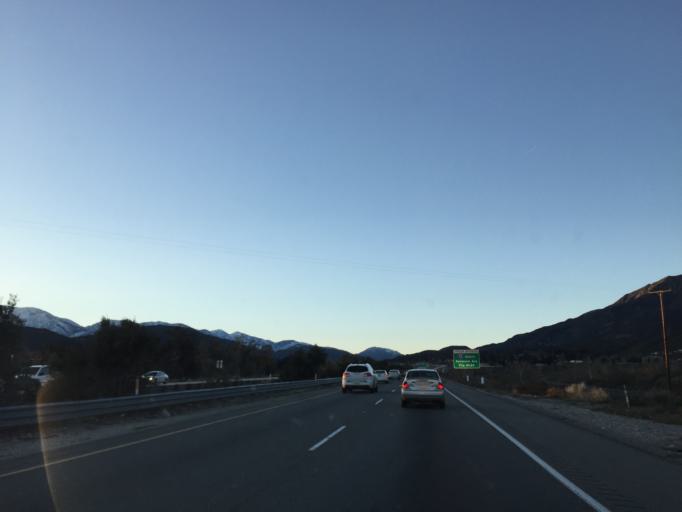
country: US
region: California
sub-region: San Bernardino County
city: Muscoy
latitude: 34.2140
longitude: -117.3910
